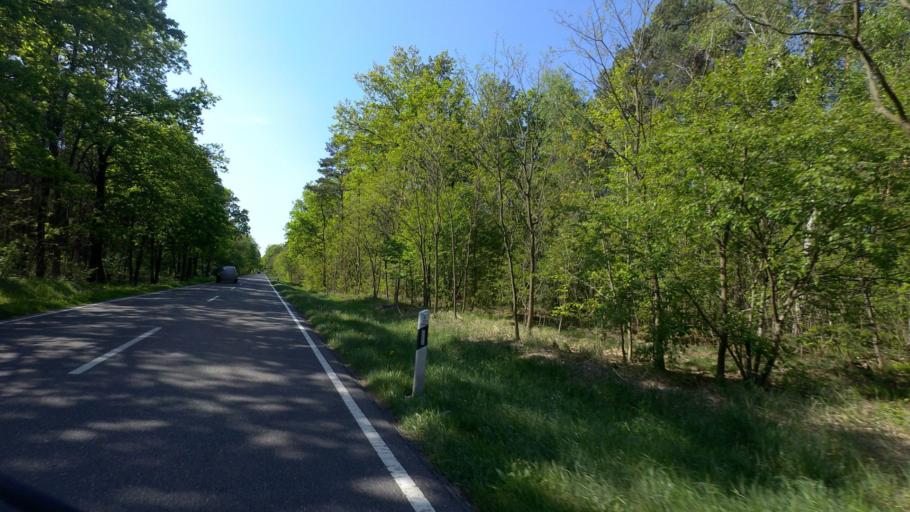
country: DE
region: Brandenburg
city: Schlepzig
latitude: 52.0674
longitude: 13.9085
